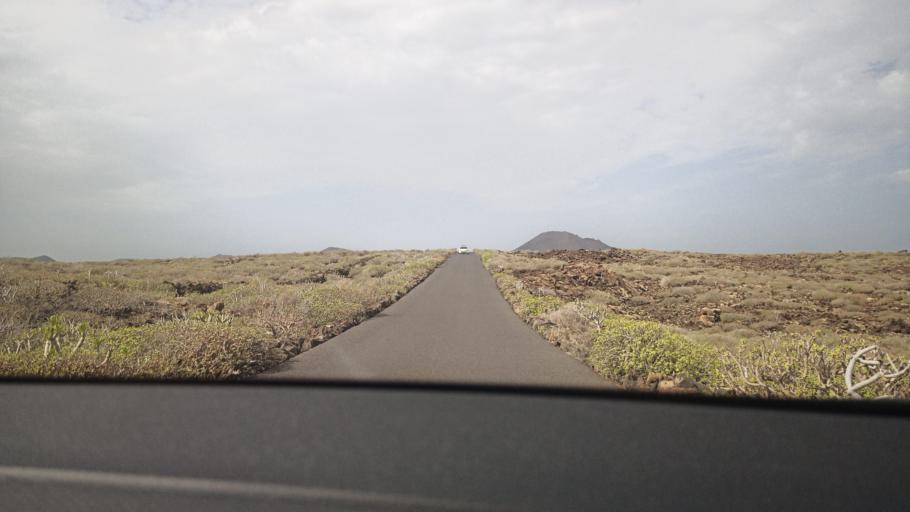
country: ES
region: Canary Islands
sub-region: Provincia de Las Palmas
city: Haria
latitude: 29.1592
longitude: -13.4361
